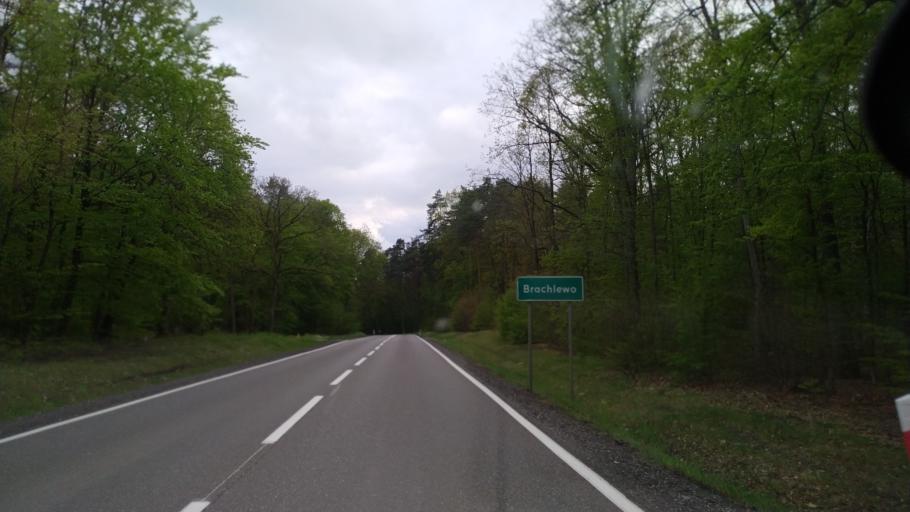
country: PL
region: Pomeranian Voivodeship
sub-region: Powiat kwidzynski
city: Ryjewo
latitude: 53.8087
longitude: 18.9666
